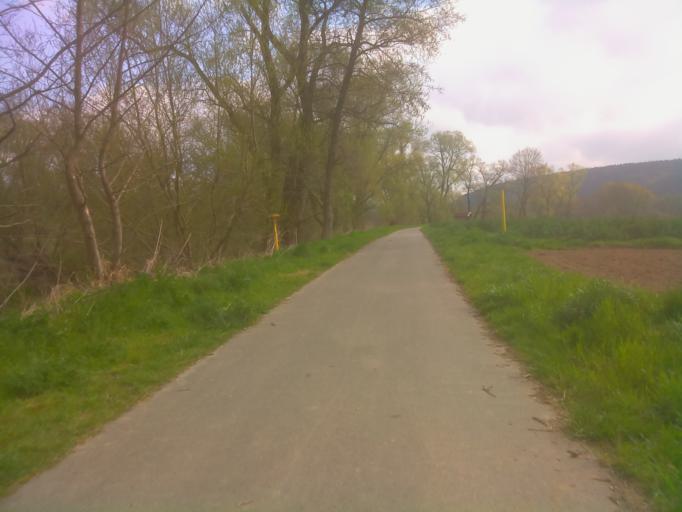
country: DE
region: Thuringia
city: Freienorla
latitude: 50.7722
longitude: 11.5445
